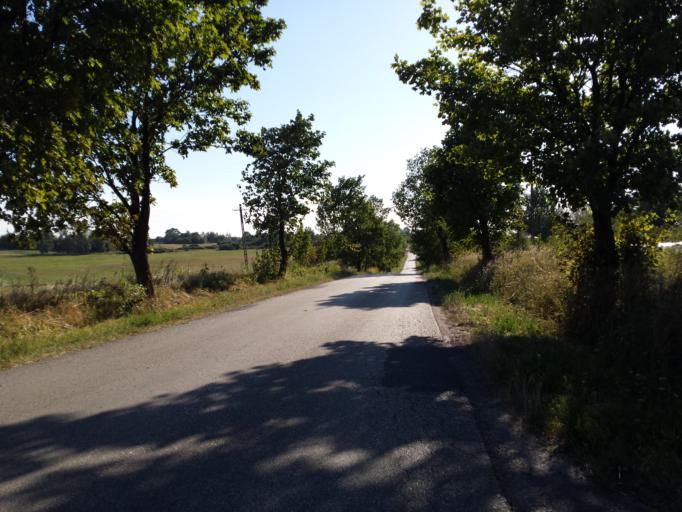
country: PL
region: Swietokrzyskie
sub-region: Powiat buski
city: Gnojno
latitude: 50.6539
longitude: 20.8277
